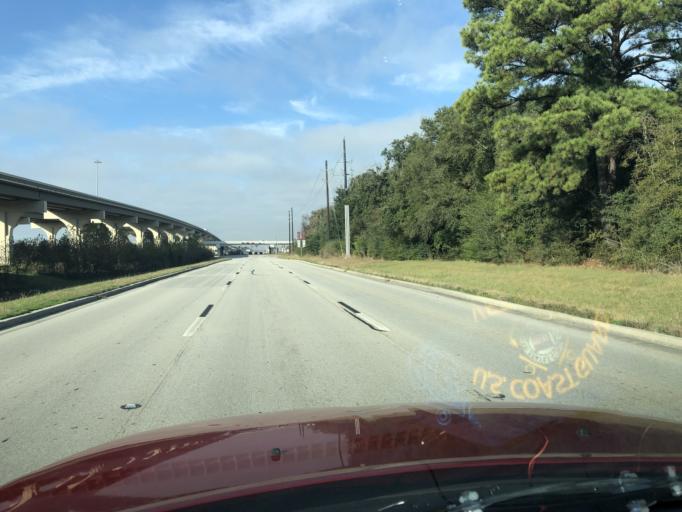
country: US
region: Texas
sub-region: Harris County
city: Tomball
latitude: 30.0523
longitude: -95.6117
